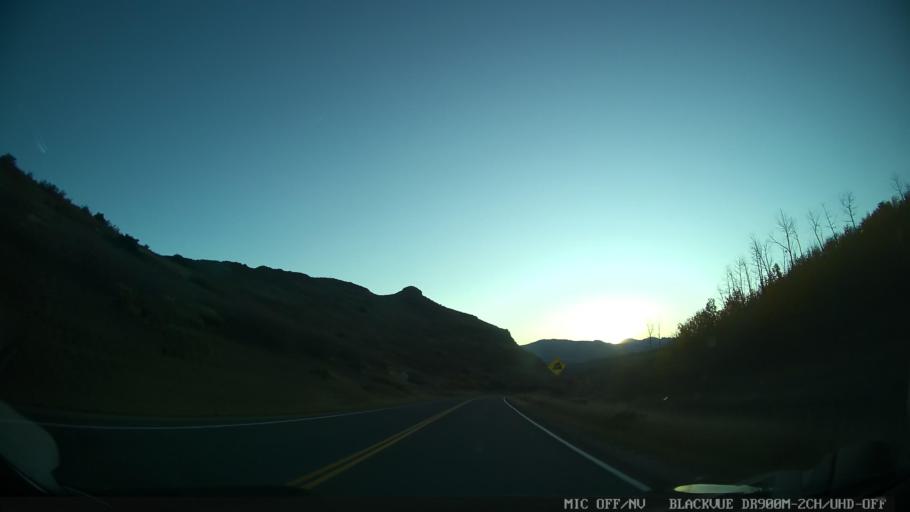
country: US
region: Colorado
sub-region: Eagle County
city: Edwards
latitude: 39.8159
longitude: -106.6729
